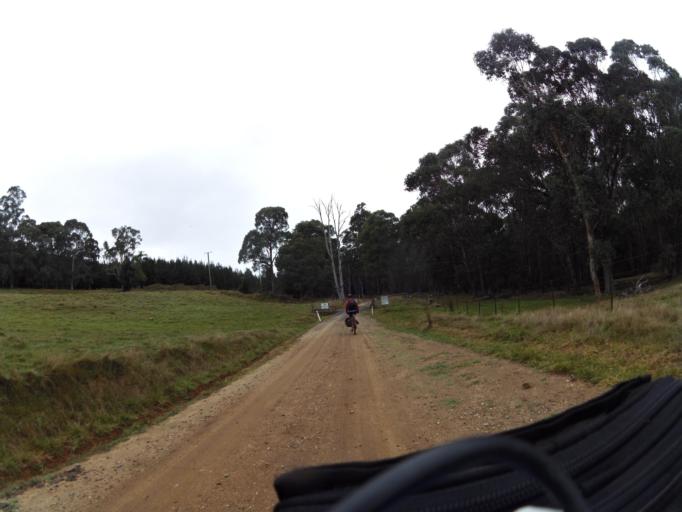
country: AU
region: New South Wales
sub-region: Greater Hume Shire
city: Holbrook
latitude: -36.1672
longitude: 147.4955
